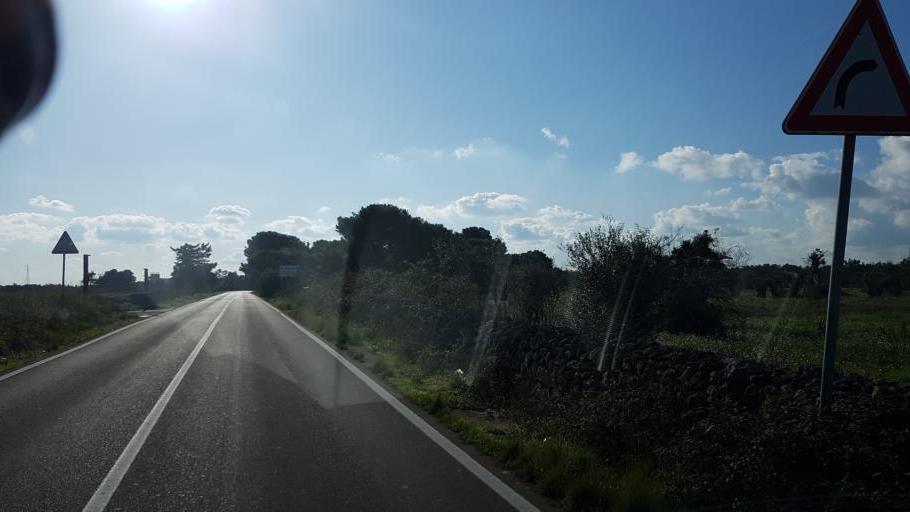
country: IT
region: Apulia
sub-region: Provincia di Lecce
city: Trepuzzi
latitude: 40.4552
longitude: 18.1128
